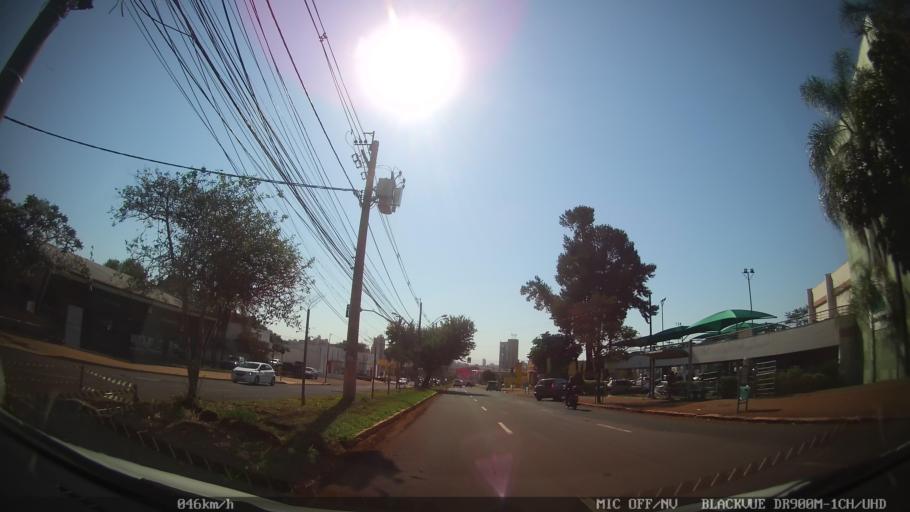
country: BR
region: Sao Paulo
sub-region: Ribeirao Preto
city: Ribeirao Preto
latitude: -21.1923
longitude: -47.8106
